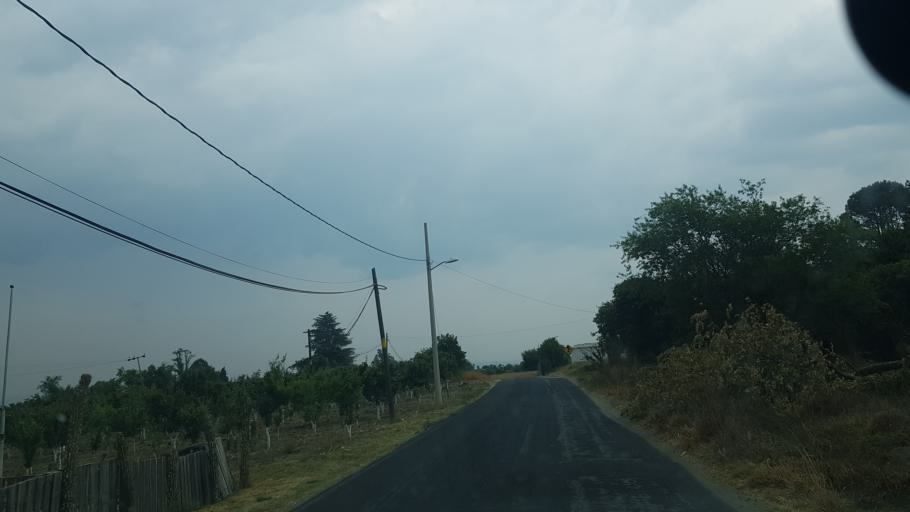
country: MX
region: Puebla
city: San Lorenzo Chiautzingo
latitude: 19.1953
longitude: -98.4650
